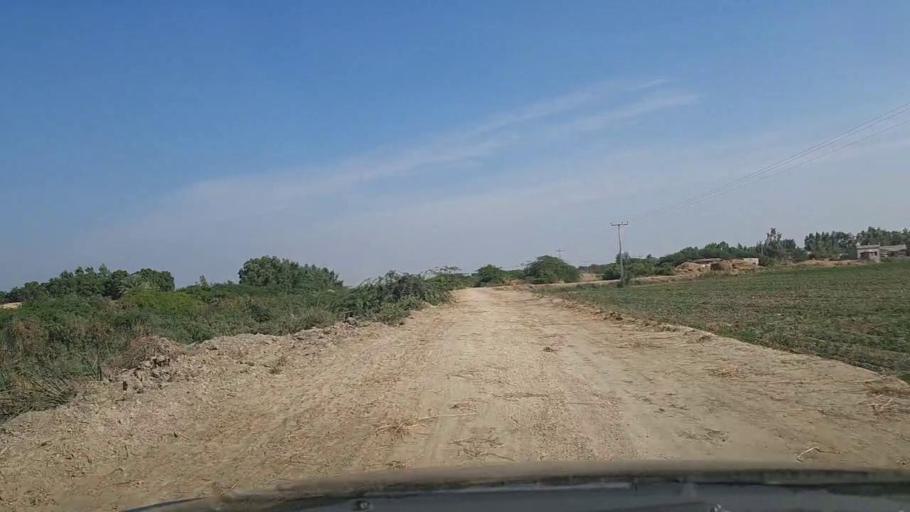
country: PK
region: Sindh
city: Thatta
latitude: 24.7112
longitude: 67.7797
